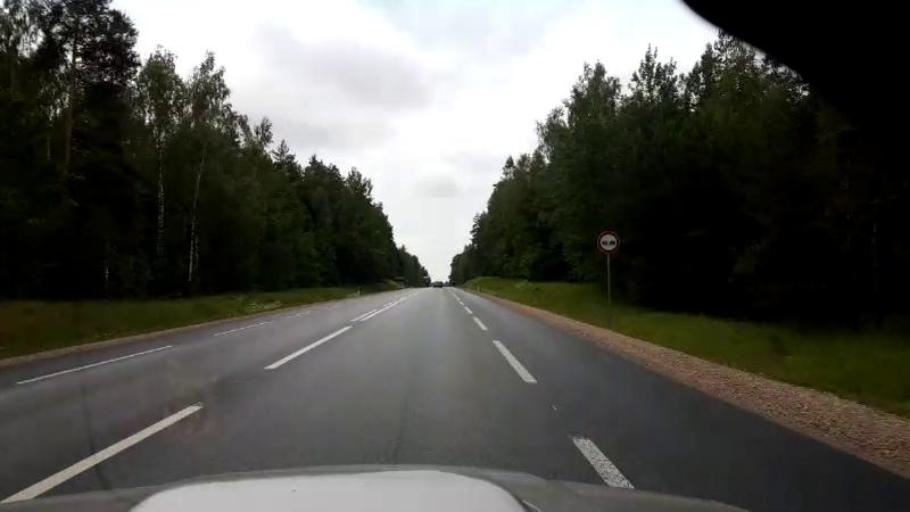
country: LV
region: Lecava
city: Iecava
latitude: 56.6660
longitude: 24.2337
